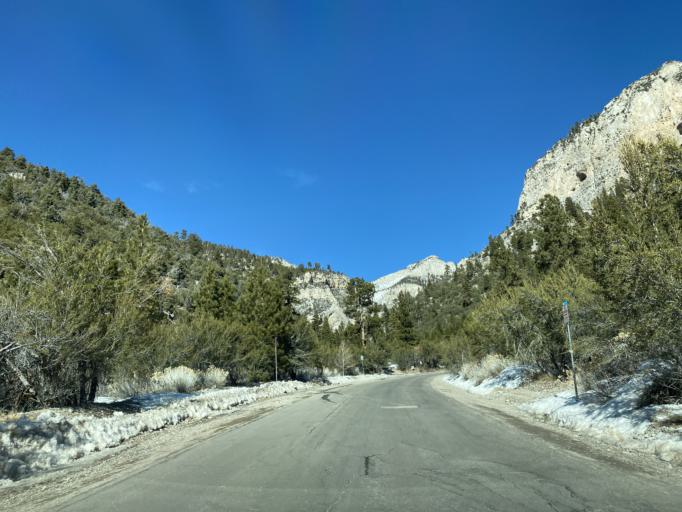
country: US
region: Nevada
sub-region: Nye County
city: Pahrump
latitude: 36.2665
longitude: -115.6583
